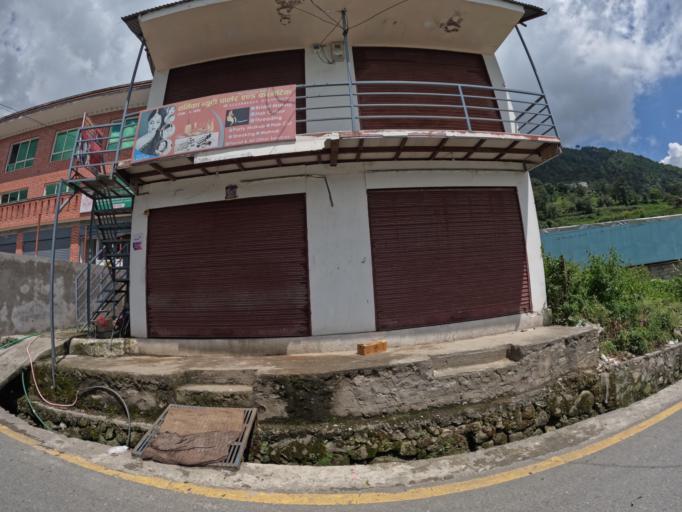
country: NP
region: Central Region
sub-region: Bagmati Zone
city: Kathmandu
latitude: 27.7918
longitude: 85.3302
